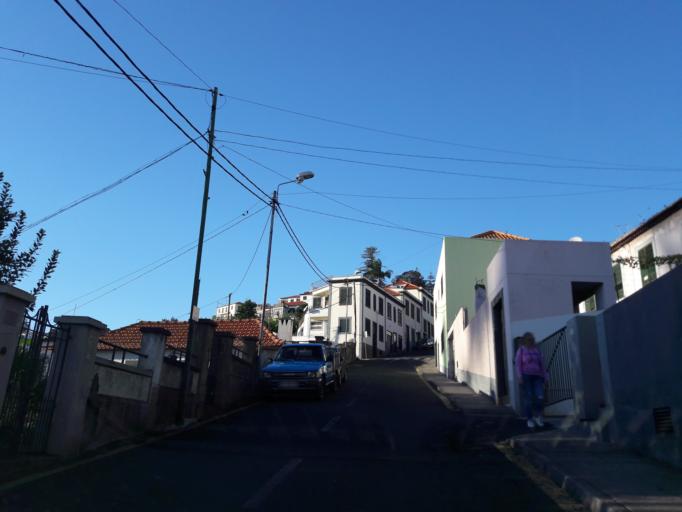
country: PT
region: Madeira
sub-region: Funchal
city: Nossa Senhora do Monte
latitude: 32.6567
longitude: -16.9151
